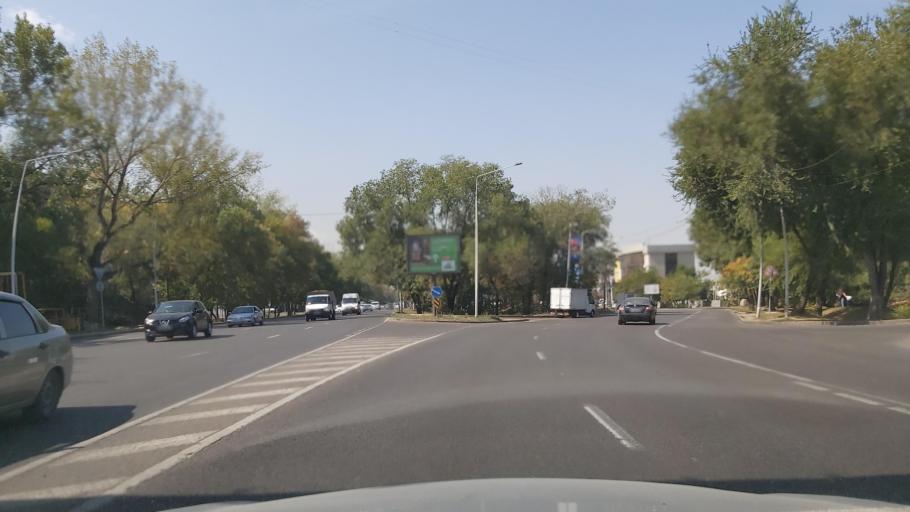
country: KZ
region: Almaty Qalasy
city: Almaty
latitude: 43.2632
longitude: 76.8998
